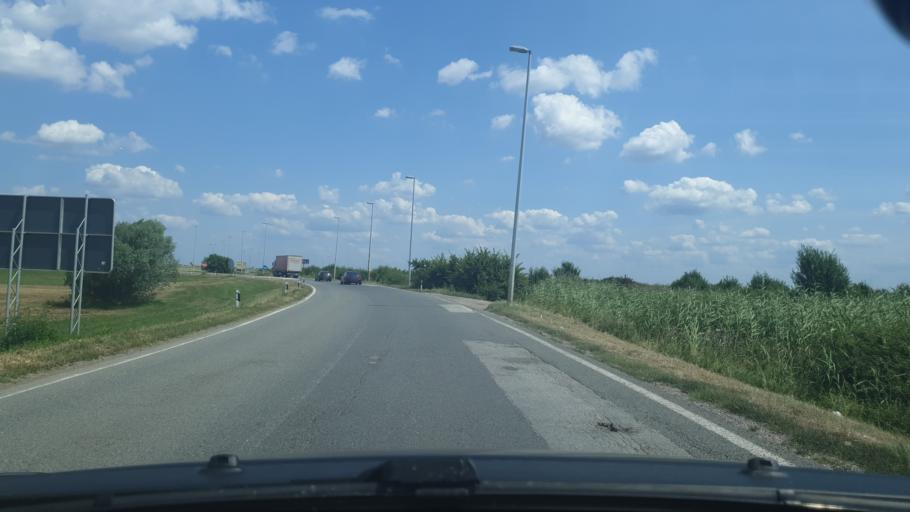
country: RS
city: Simanovci
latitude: 44.8755
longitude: 20.1227
